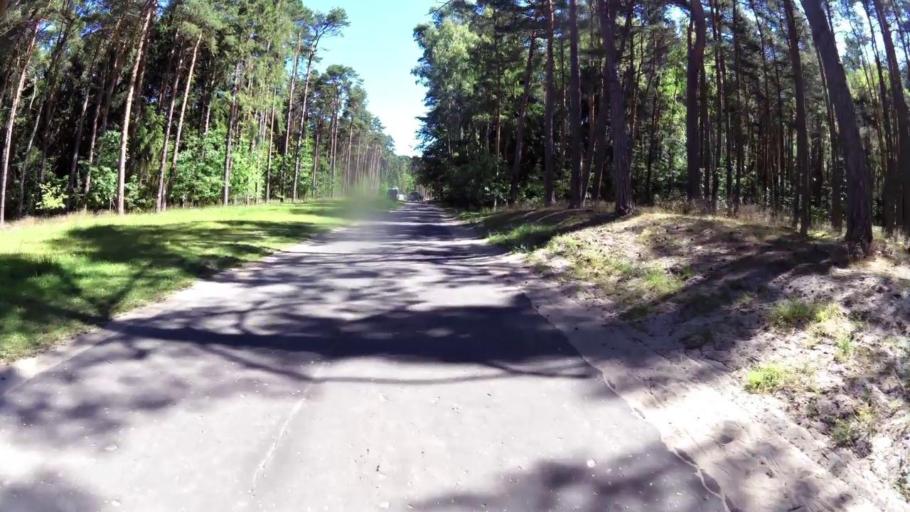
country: PL
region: West Pomeranian Voivodeship
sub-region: Powiat gryficki
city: Pobierowo
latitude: 54.0469
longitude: 14.8762
